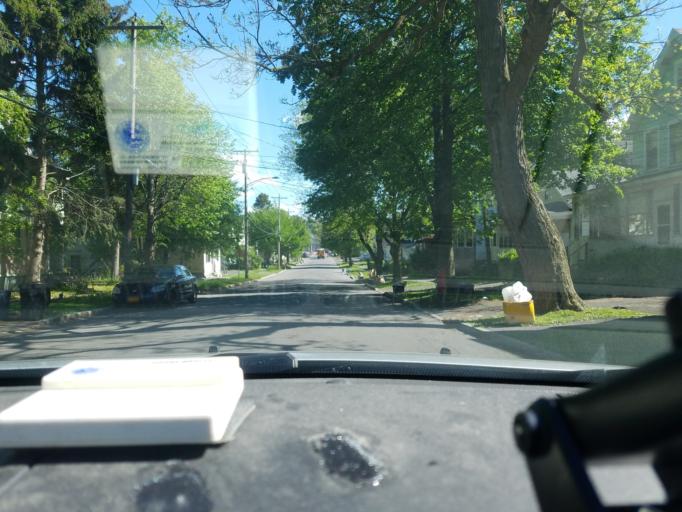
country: US
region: New York
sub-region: Onondaga County
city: Syracuse
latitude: 43.0548
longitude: -76.1303
